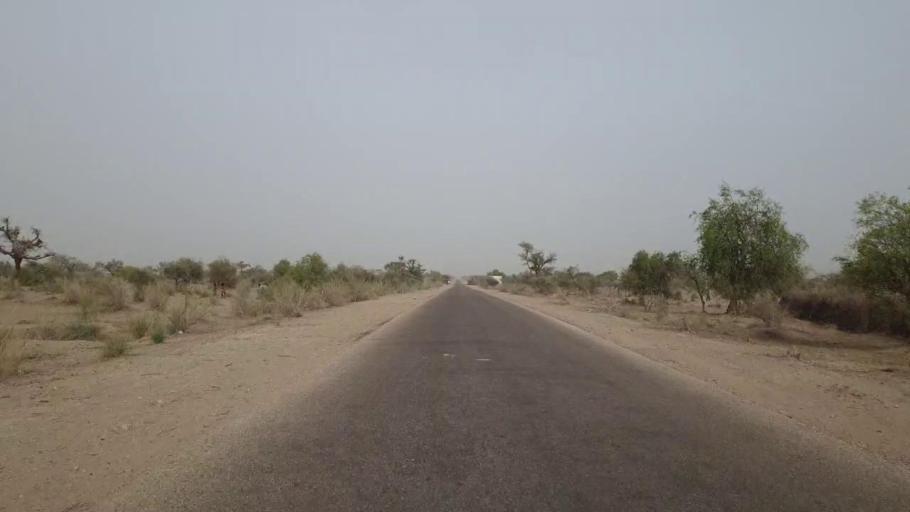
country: PK
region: Sindh
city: Islamkot
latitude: 24.5753
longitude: 70.3132
